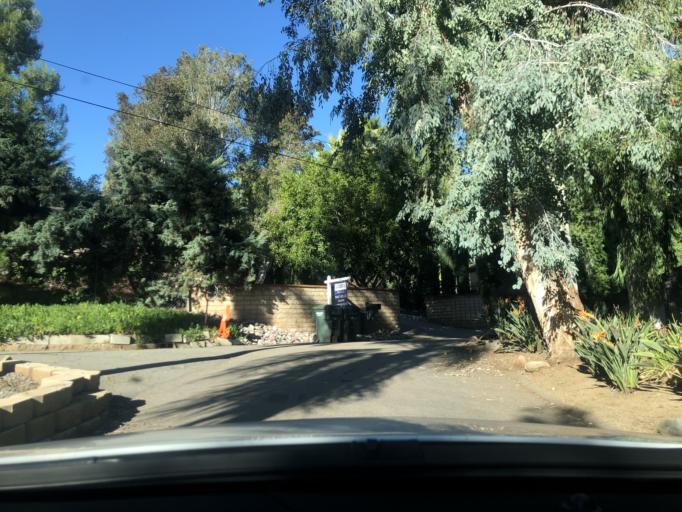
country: US
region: California
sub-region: San Diego County
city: Rancho San Diego
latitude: 32.7671
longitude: -116.9385
